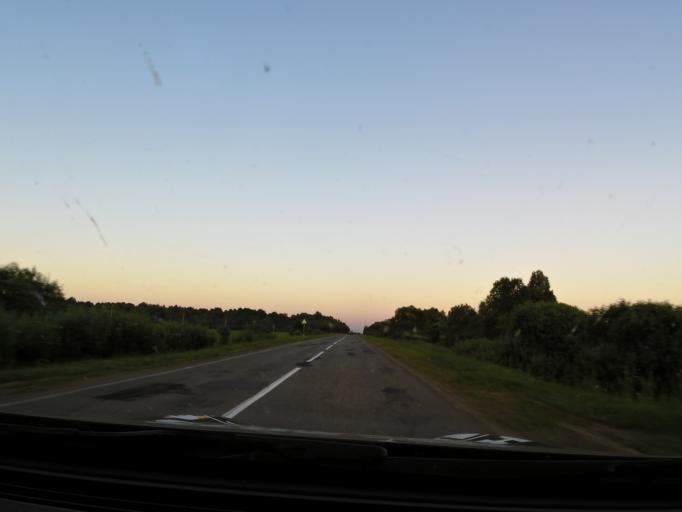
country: RU
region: Jaroslavl
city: Lyubim
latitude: 58.3284
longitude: 40.9108
